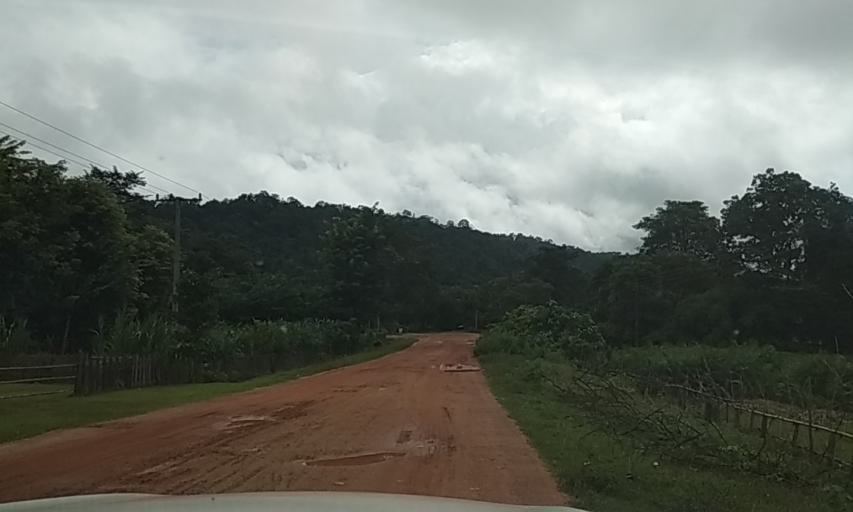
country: LA
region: Bolikhamxai
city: Bolikhan
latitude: 18.5571
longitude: 103.7405
